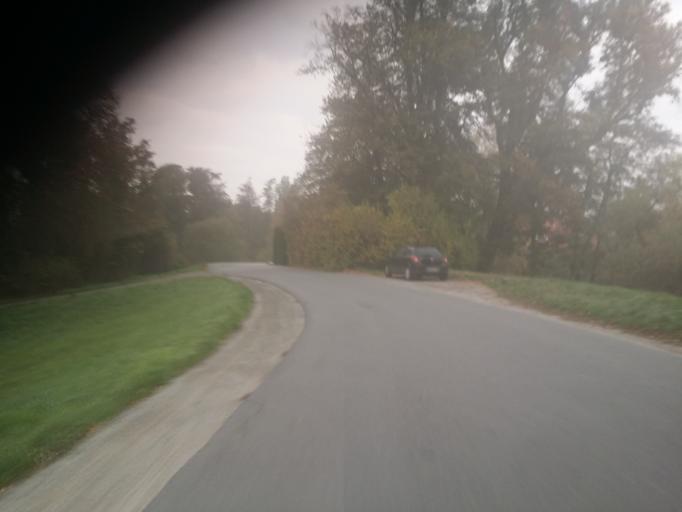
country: DE
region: Lower Saxony
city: Lilienthal
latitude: 53.1314
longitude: 8.8619
